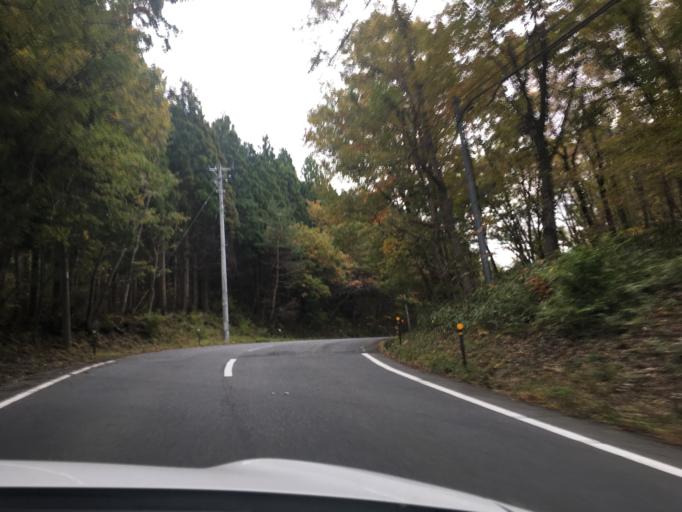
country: JP
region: Fukushima
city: Iwaki
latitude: 37.1107
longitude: 140.7806
